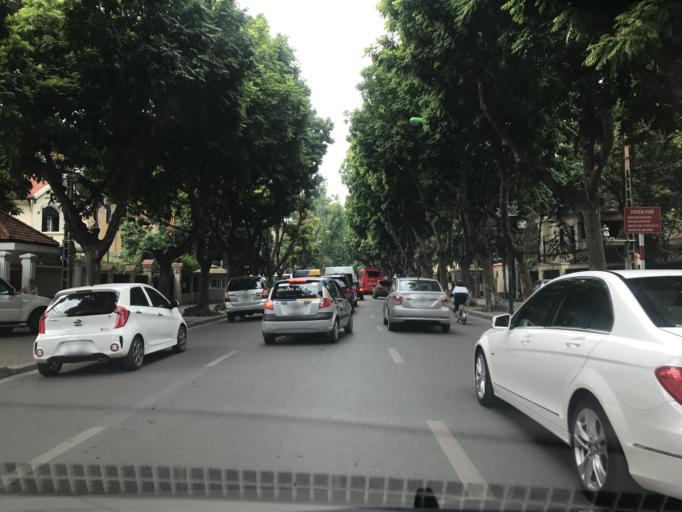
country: VN
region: Ha Noi
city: Hanoi
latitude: 21.0314
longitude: 105.8372
